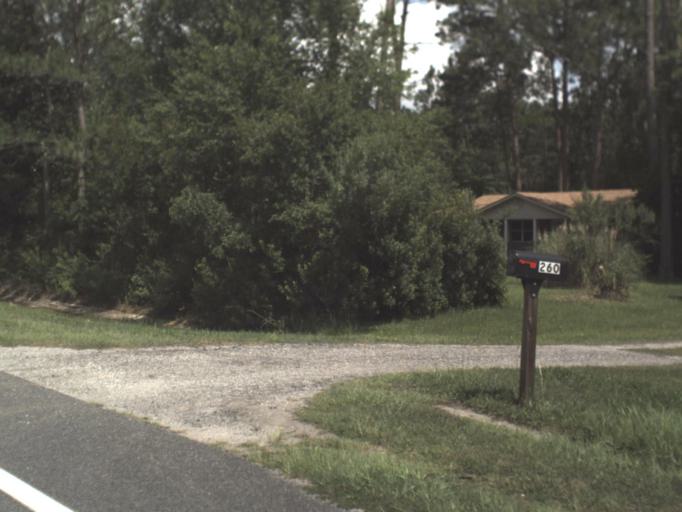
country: US
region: Florida
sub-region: Bradford County
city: Starke
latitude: 29.9564
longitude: -82.0497
